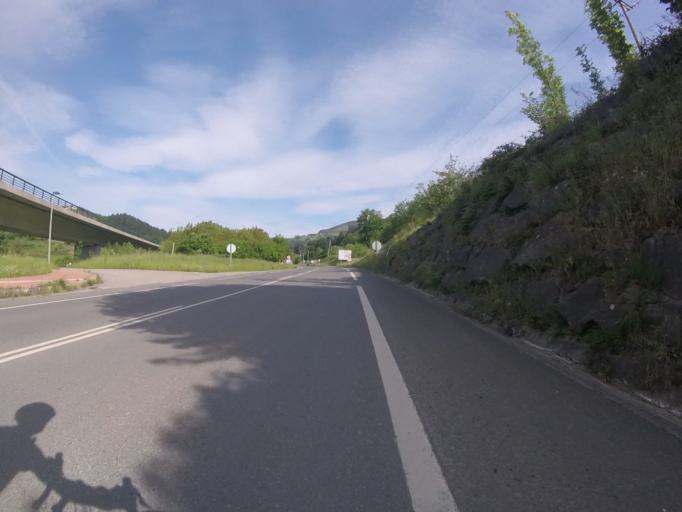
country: ES
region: Basque Country
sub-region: Provincia de Guipuzcoa
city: Gabiria
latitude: 43.0743
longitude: -2.2893
